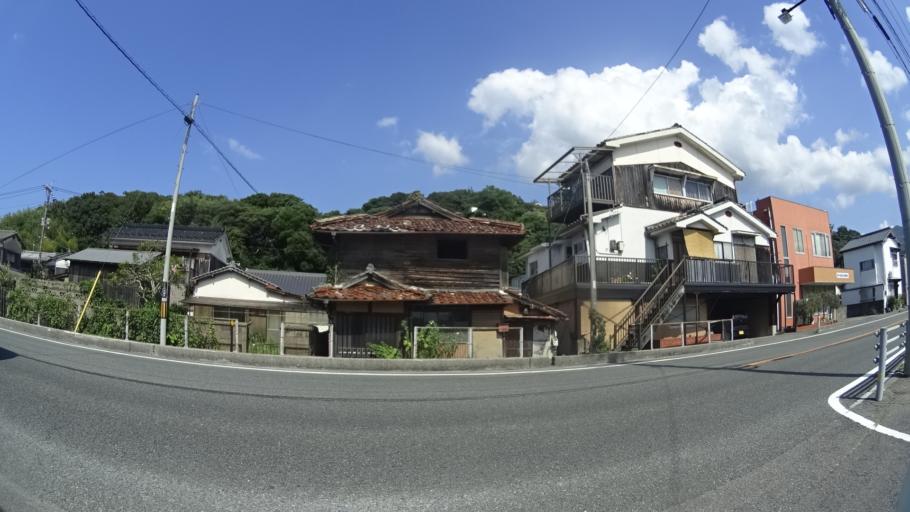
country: JP
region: Yamaguchi
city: Hagi
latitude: 34.4314
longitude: 131.4152
